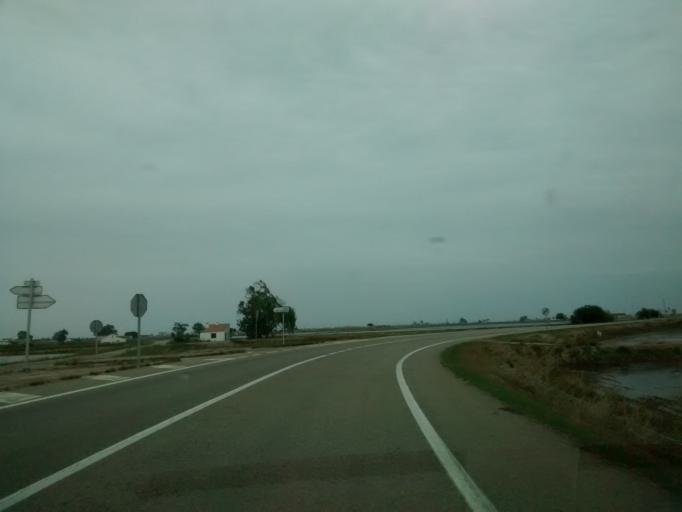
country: ES
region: Catalonia
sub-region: Provincia de Tarragona
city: Deltebre
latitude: 40.7003
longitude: 0.6769
